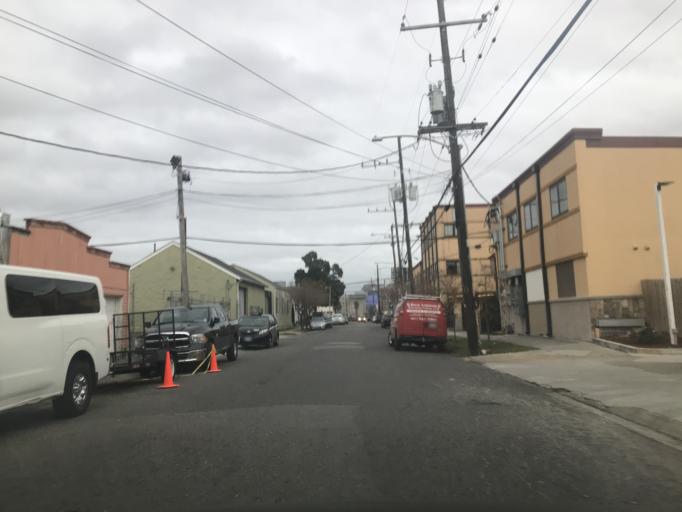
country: US
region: Louisiana
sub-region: Orleans Parish
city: New Orleans
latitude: 29.9655
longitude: -90.0975
